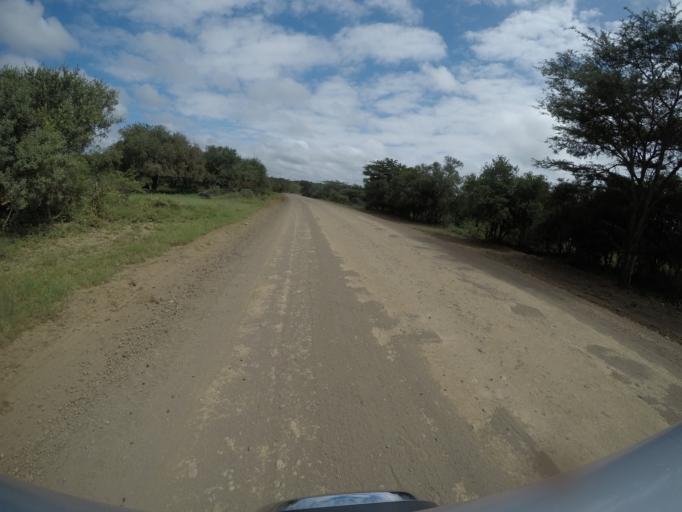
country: ZA
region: KwaZulu-Natal
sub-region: uThungulu District Municipality
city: Empangeni
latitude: -28.6188
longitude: 31.8538
